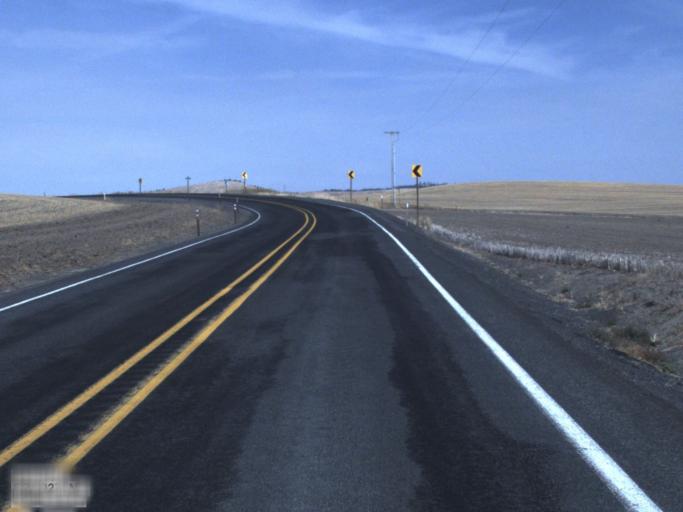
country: US
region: Idaho
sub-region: Benewah County
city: Plummer
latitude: 47.2731
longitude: -117.1315
